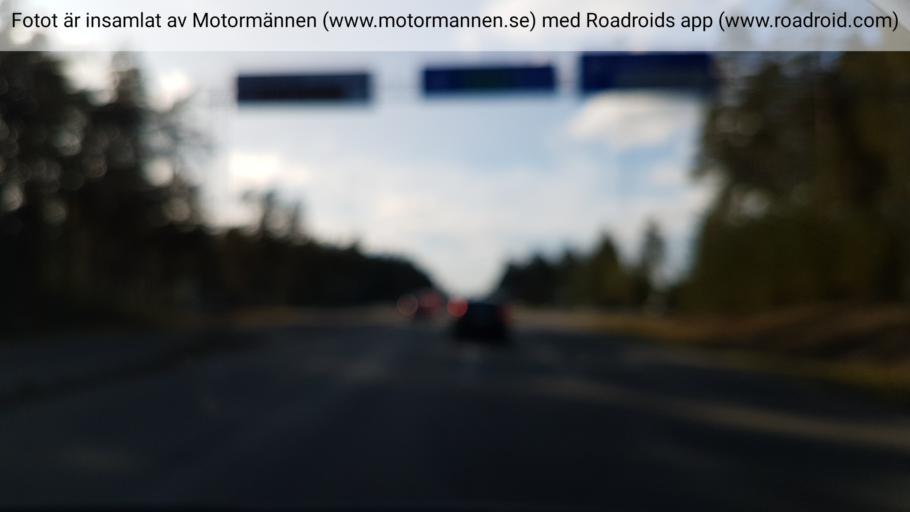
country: SE
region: Vaesterbotten
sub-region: Umea Kommun
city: Roback
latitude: 63.8451
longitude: 20.1623
